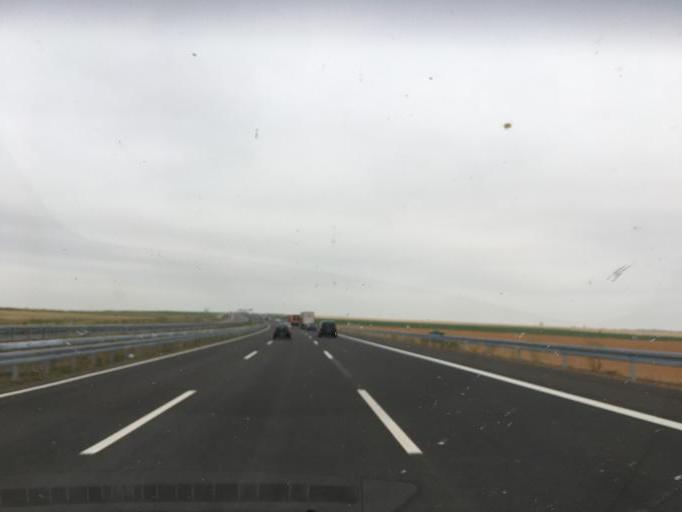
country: DE
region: North Rhine-Westphalia
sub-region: Regierungsbezirk Dusseldorf
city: Juchen
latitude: 51.0580
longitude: 6.4985
